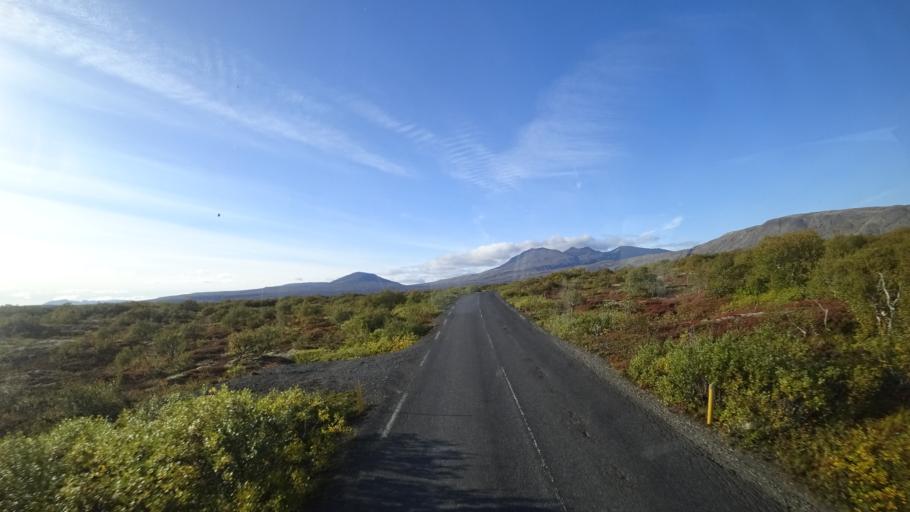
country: IS
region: South
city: Hveragerdi
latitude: 64.2667
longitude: -21.0609
